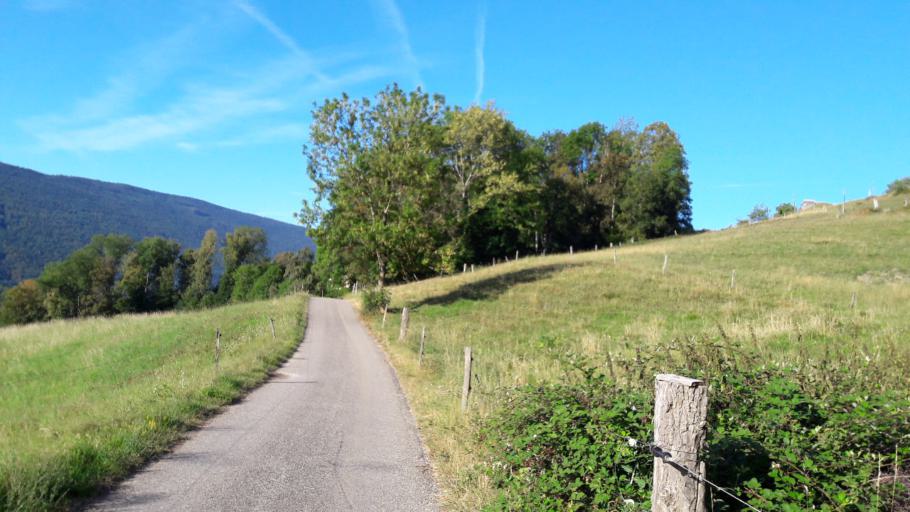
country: CH
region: Solothurn
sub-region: Bezirk Thal
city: Balsthal
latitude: 47.3233
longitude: 7.6785
